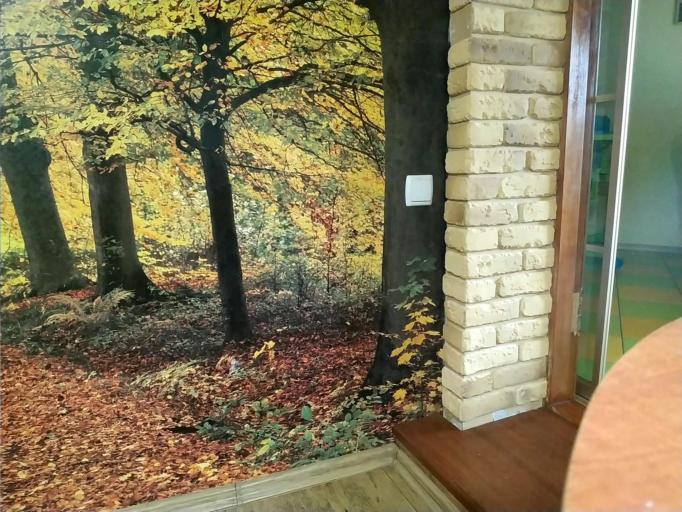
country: RU
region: Smolensk
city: Dorogobuzh
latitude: 54.9738
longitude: 33.2758
